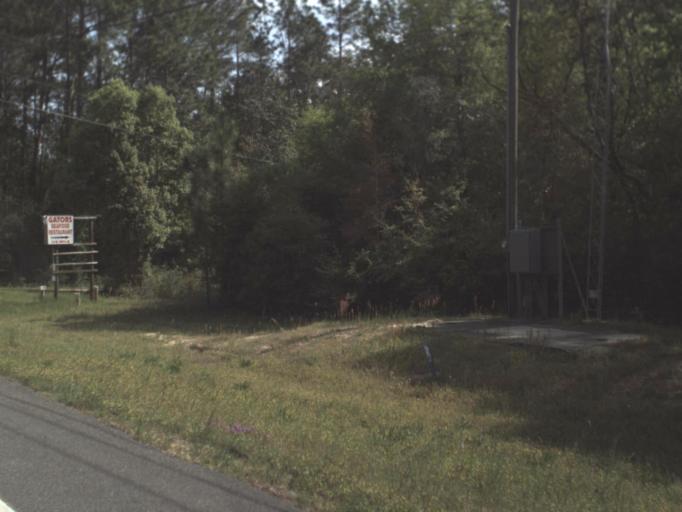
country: US
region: Florida
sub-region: Santa Rosa County
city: East Milton
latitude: 30.5875
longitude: -86.9338
